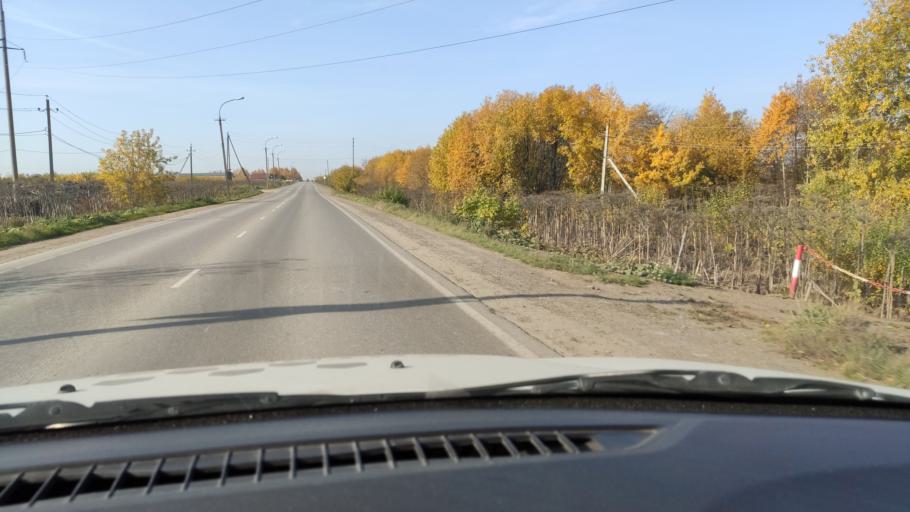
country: RU
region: Perm
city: Sylva
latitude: 58.0276
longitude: 56.7207
